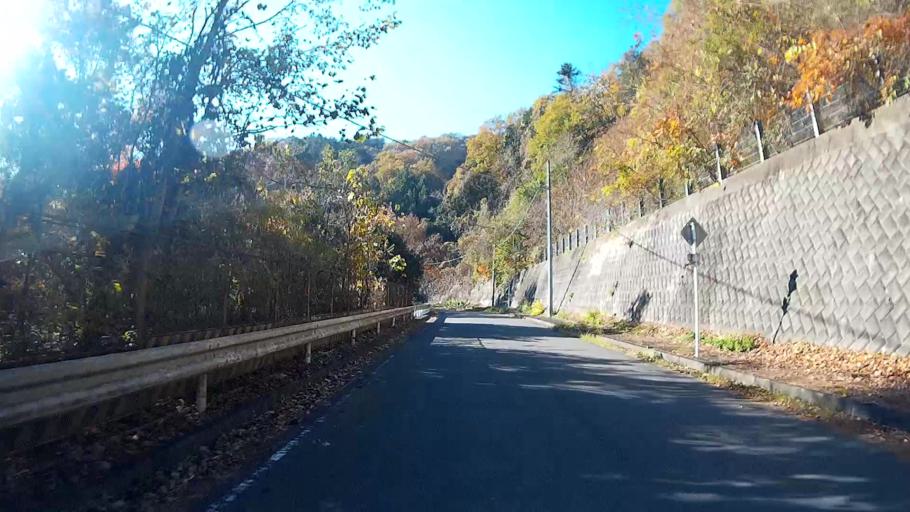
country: JP
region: Yamanashi
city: Uenohara
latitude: 35.5915
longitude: 139.1287
